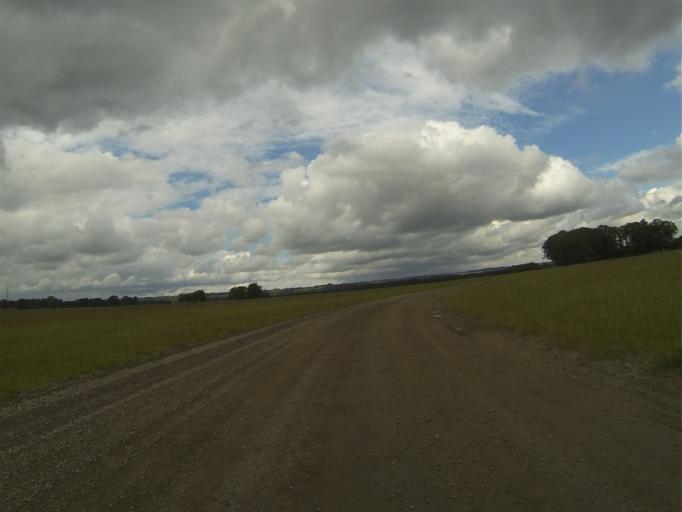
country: SE
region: Skane
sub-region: Lunds Kommun
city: Veberod
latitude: 55.7071
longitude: 13.4405
